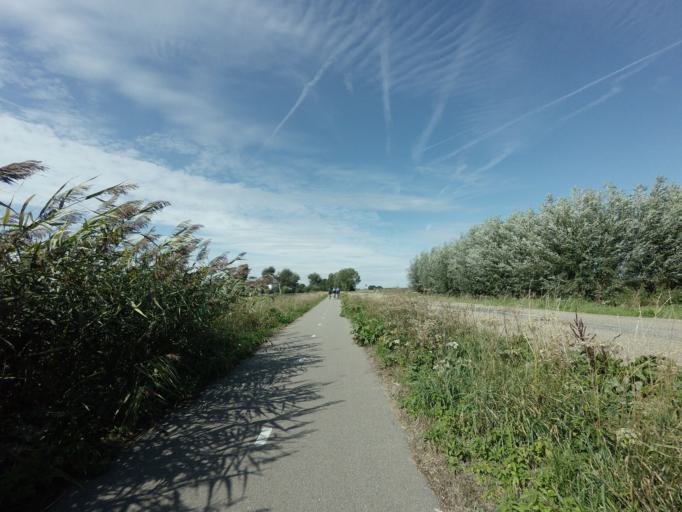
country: NL
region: Utrecht
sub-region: Gemeente De Ronde Venen
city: Mijdrecht
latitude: 52.2117
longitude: 4.8525
